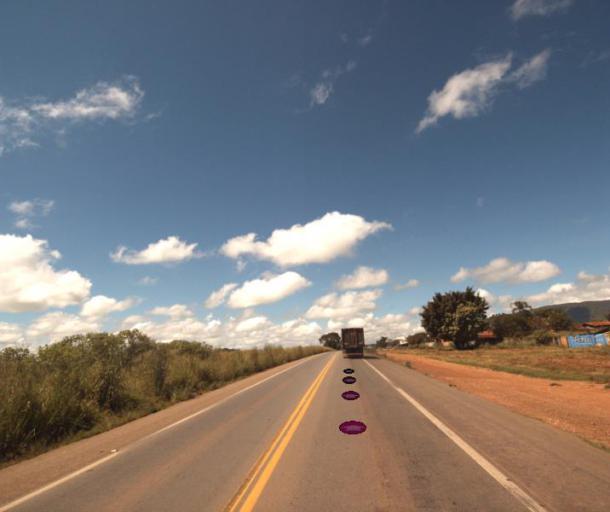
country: BR
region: Goias
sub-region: Jaragua
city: Jaragua
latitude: -15.7512
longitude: -49.3165
